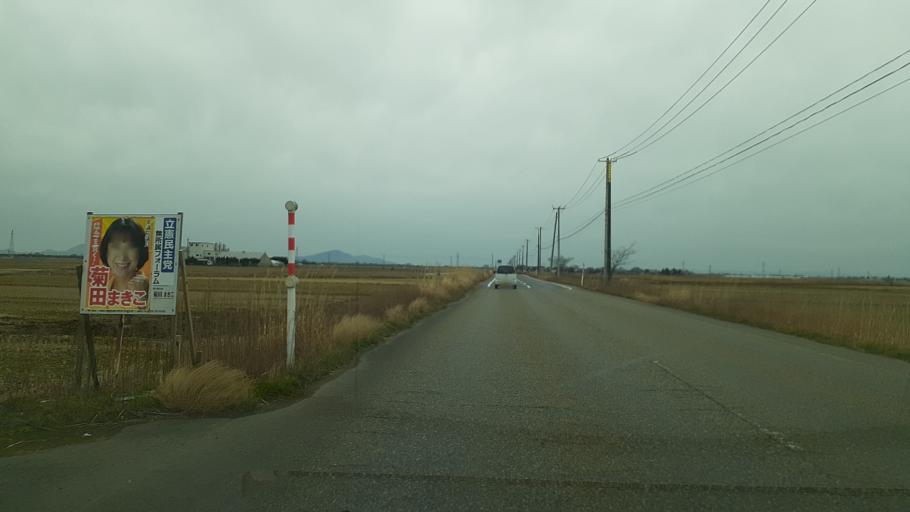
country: JP
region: Niigata
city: Niitsu-honcho
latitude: 37.8159
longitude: 139.0908
